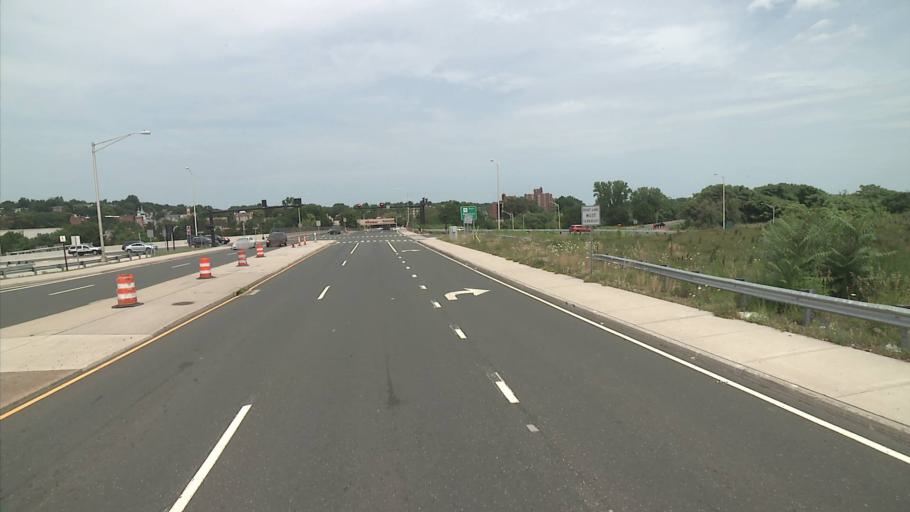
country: US
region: Connecticut
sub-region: Hartford County
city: New Britain
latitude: 41.6684
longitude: -72.7780
